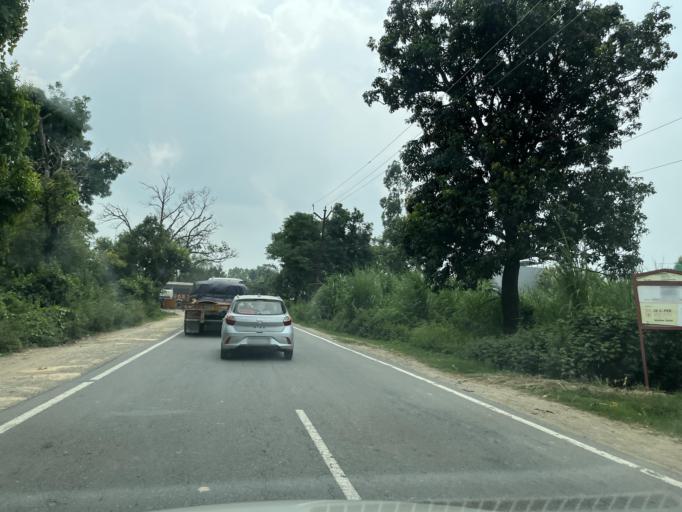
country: IN
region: Uttar Pradesh
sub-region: Bijnor
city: Najibabad
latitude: 29.5903
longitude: 78.3390
